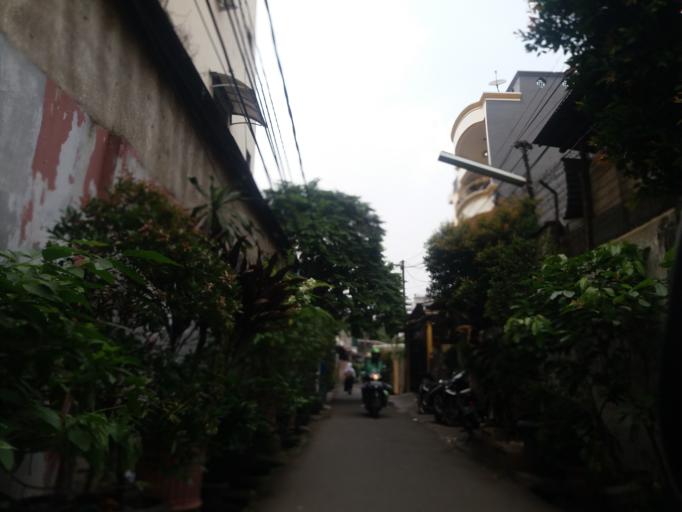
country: ID
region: Jakarta Raya
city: Jakarta
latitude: -6.1889
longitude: 106.8188
